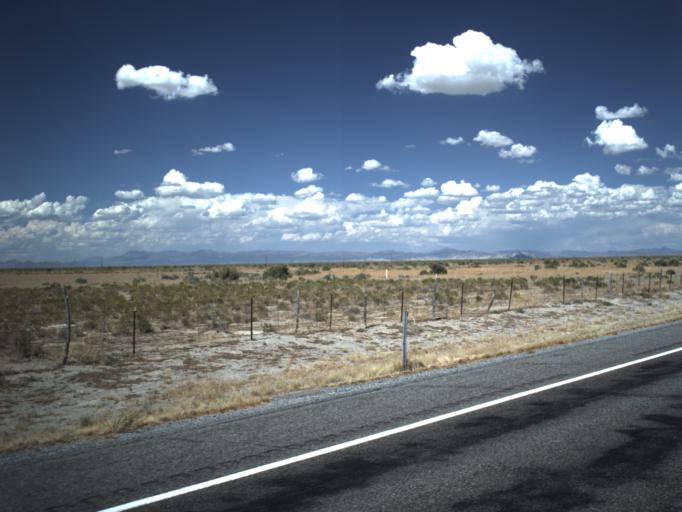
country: US
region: Utah
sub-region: Millard County
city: Delta
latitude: 39.3905
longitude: -112.5118
